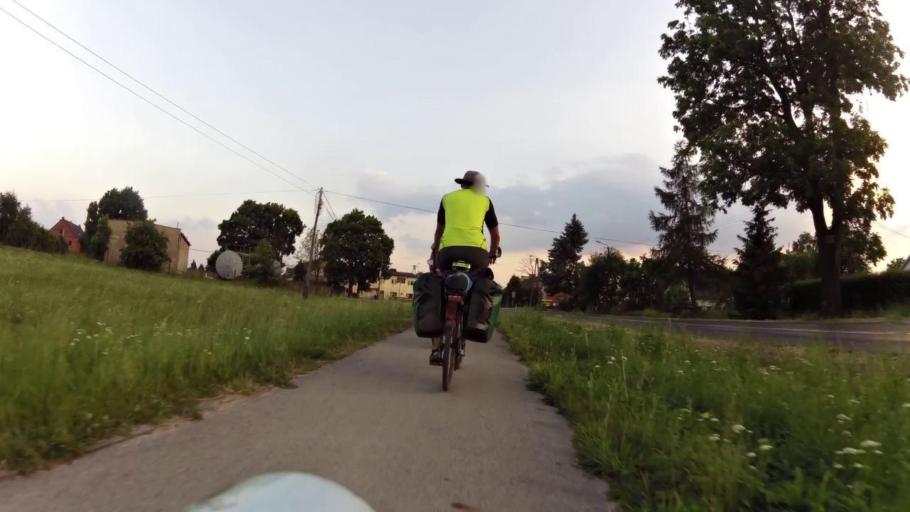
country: PL
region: Kujawsko-Pomorskie
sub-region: Bydgoszcz
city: Fordon
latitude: 53.1568
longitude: 18.2357
